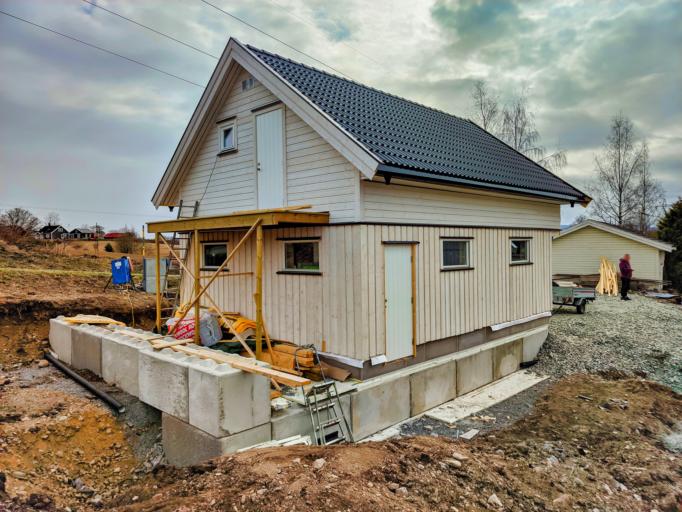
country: NO
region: Oppland
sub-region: Ostre Toten
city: Lena
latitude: 60.6929
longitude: 10.7903
